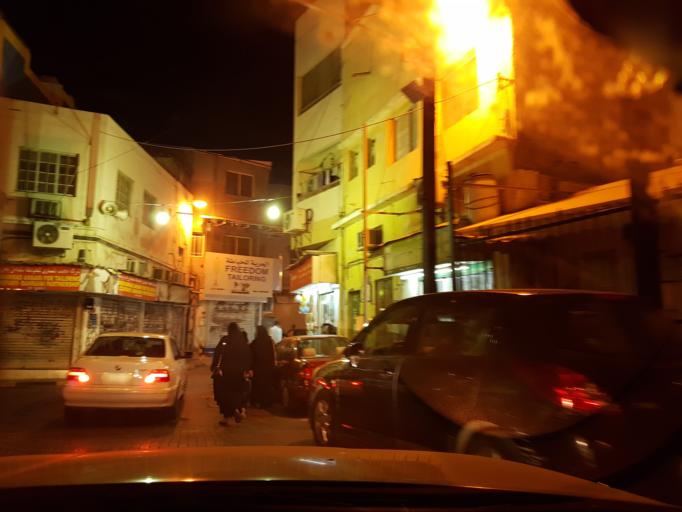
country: BH
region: Manama
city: Manama
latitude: 26.2305
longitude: 50.5779
